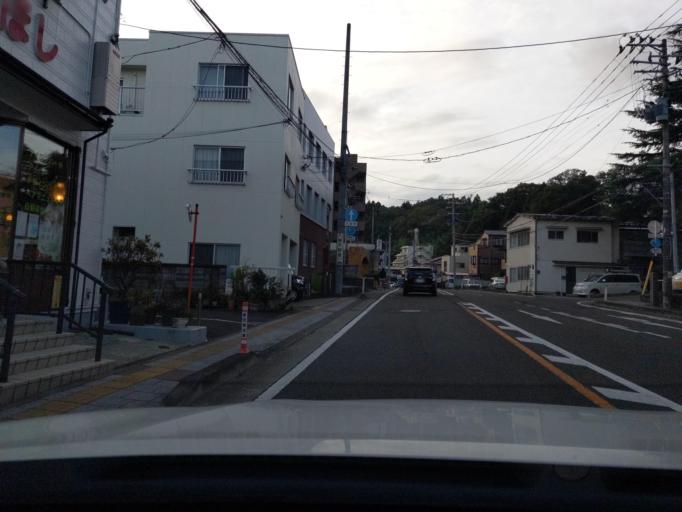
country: JP
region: Miyagi
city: Sendai
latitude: 38.2700
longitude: 140.8430
